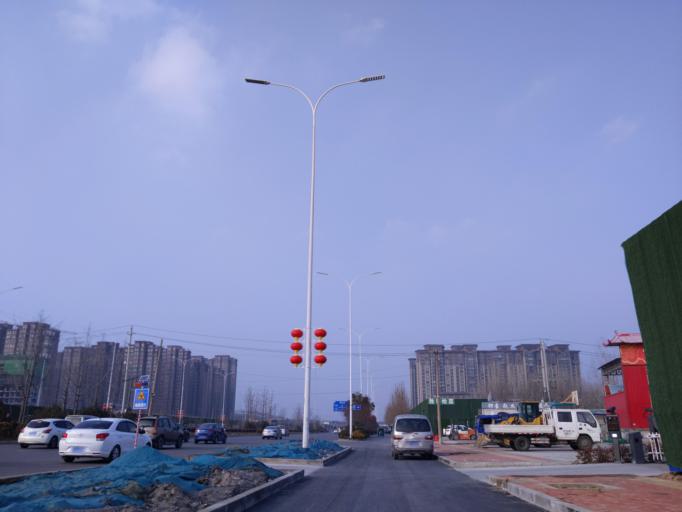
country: CN
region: Henan Sheng
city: Puyang
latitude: 35.8108
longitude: 115.0224
